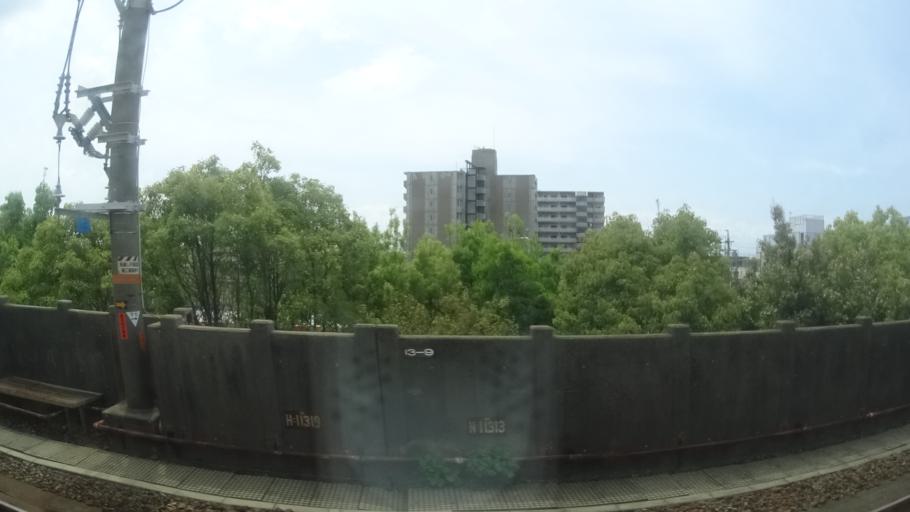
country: JP
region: Shizuoka
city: Hamamatsu
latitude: 34.6968
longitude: 137.7228
